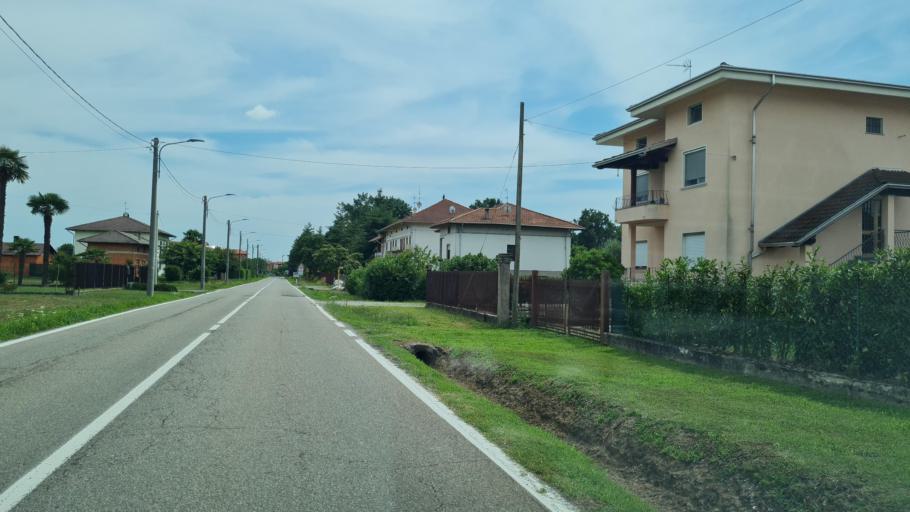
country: IT
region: Piedmont
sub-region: Provincia di Biella
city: Castelletto Cervo
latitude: 45.5438
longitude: 8.2136
